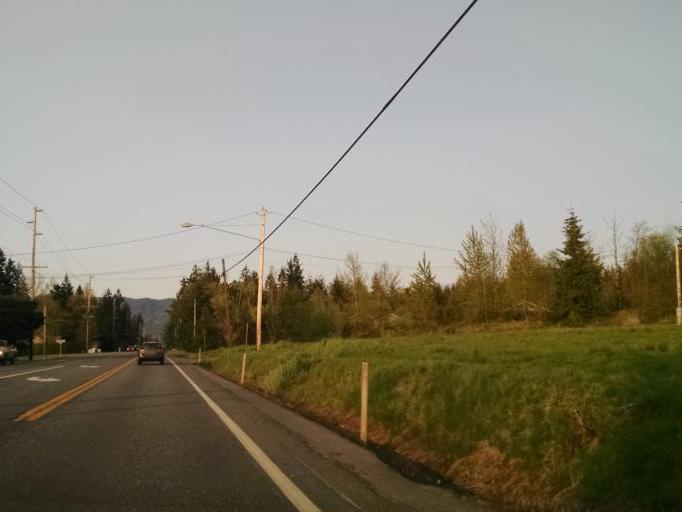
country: US
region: Washington
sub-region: Whatcom County
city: Sudden Valley
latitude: 48.8145
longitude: -122.3326
